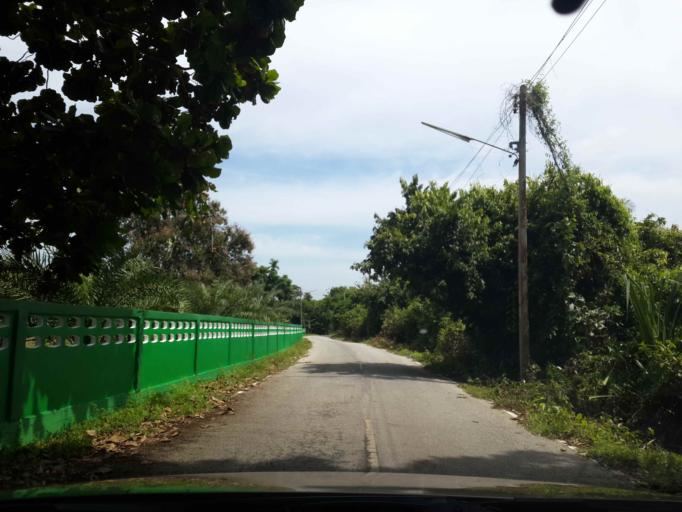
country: TH
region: Narathiwat
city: Rueso
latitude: 6.4006
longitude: 101.5161
